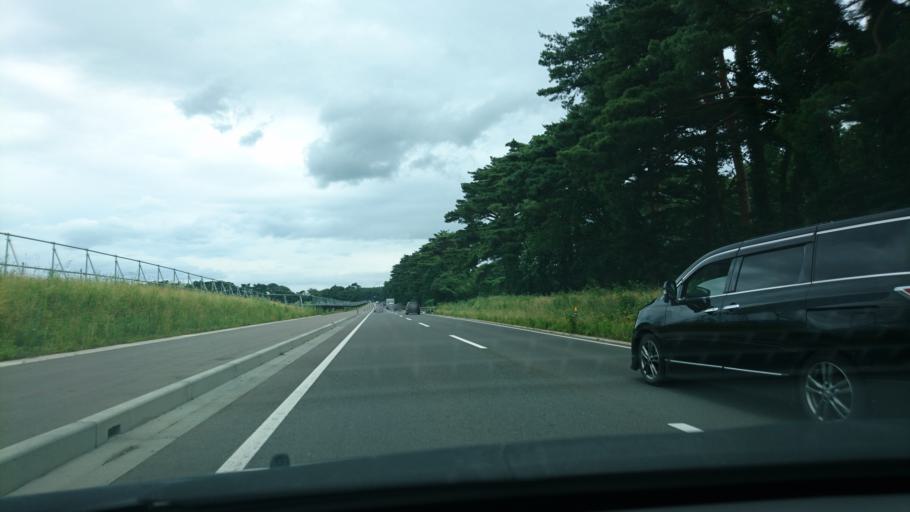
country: JP
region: Iwate
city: Morioka-shi
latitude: 39.7780
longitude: 141.1260
